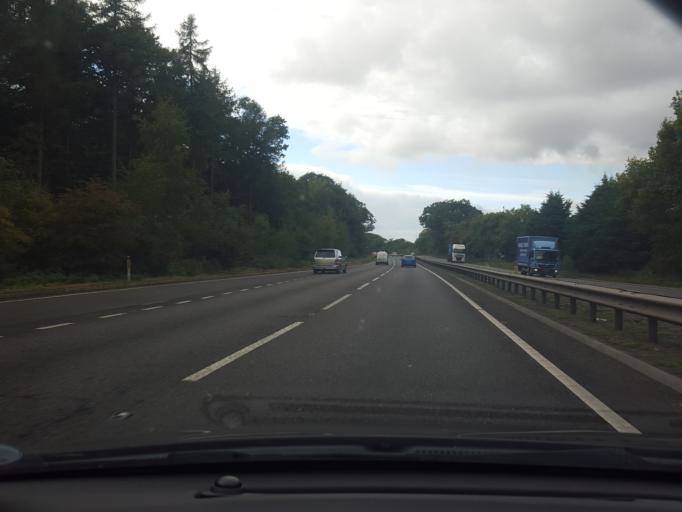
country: GB
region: England
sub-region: Suffolk
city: Thurston
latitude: 52.2386
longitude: 0.7785
